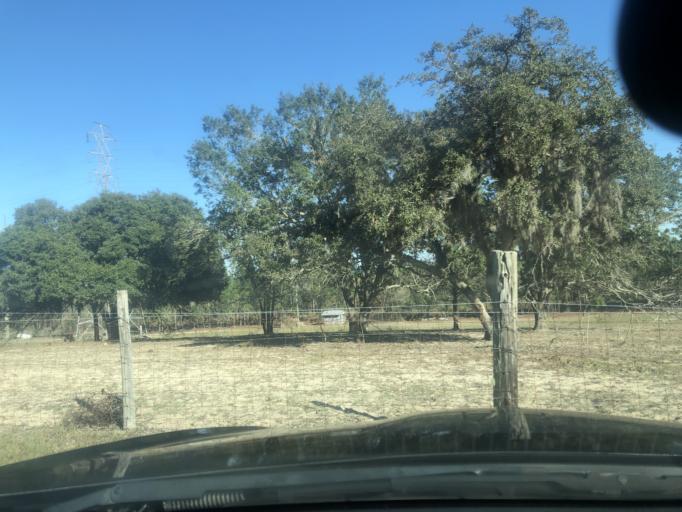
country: US
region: Florida
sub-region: Citrus County
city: Lecanto
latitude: 28.8170
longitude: -82.5180
